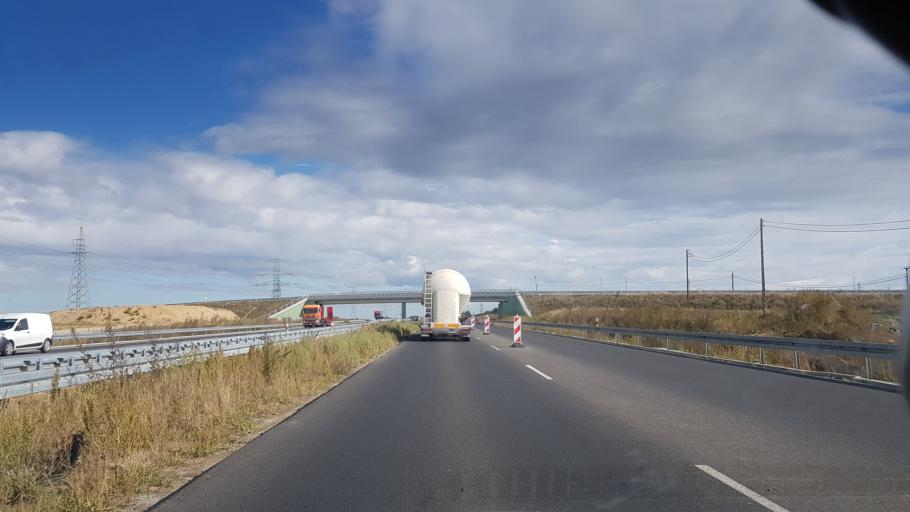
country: PL
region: Greater Poland Voivodeship
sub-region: Powiat poznanski
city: Steszew
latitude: 52.3034
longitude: 16.6978
